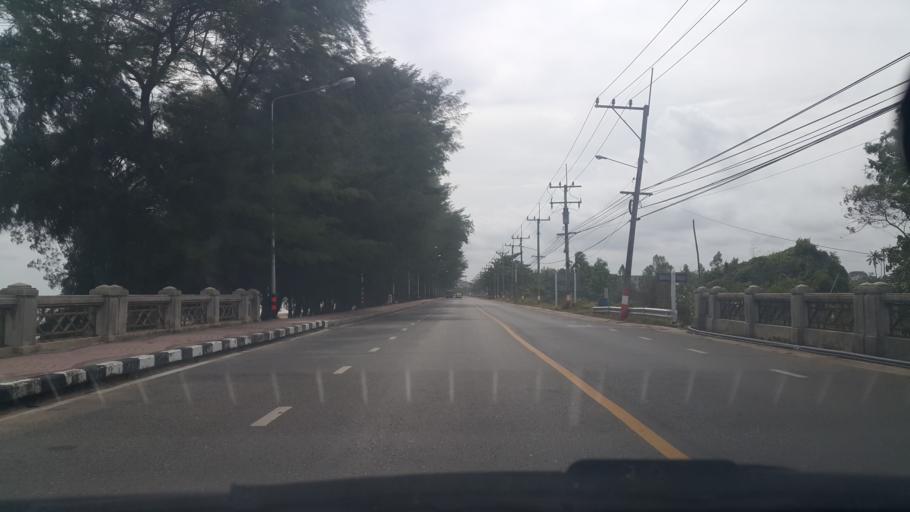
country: TH
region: Rayong
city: Rayong
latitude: 12.6196
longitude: 101.3696
